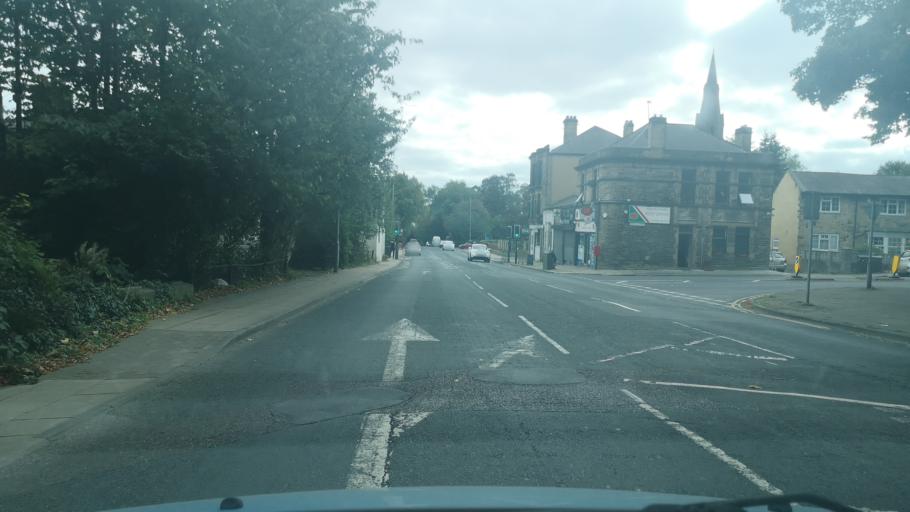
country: GB
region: England
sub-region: Kirklees
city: Batley
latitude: 53.6987
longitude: -1.6399
